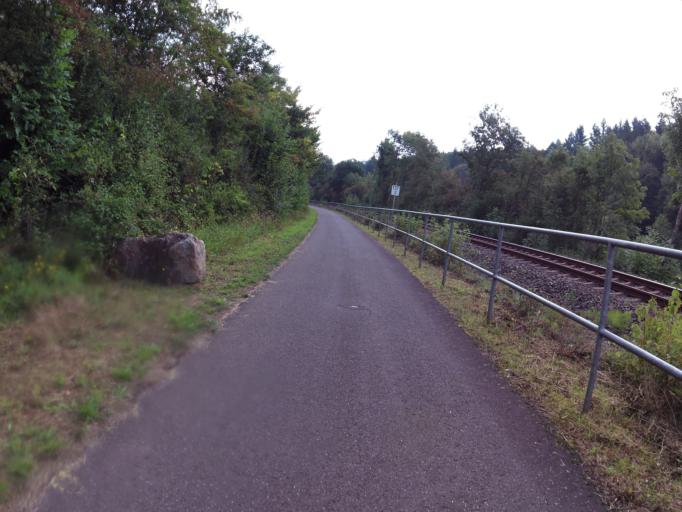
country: DE
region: Rheinland-Pfalz
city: Gondorf
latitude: 49.9571
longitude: 6.6006
